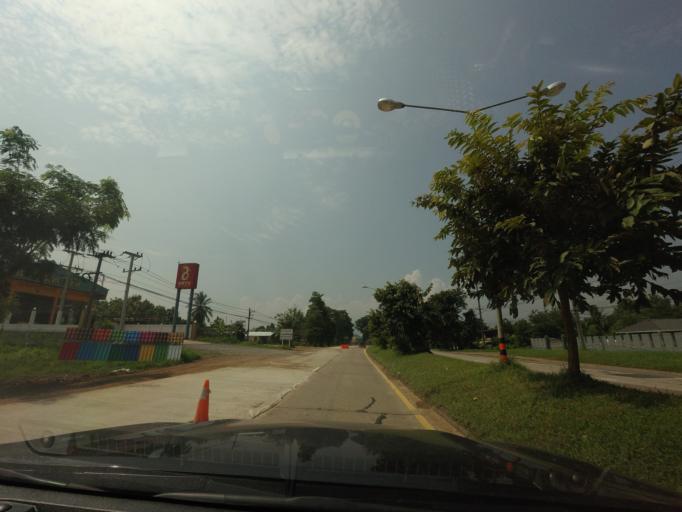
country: TH
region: Phrae
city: Den Chai
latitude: 17.9779
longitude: 100.0893
